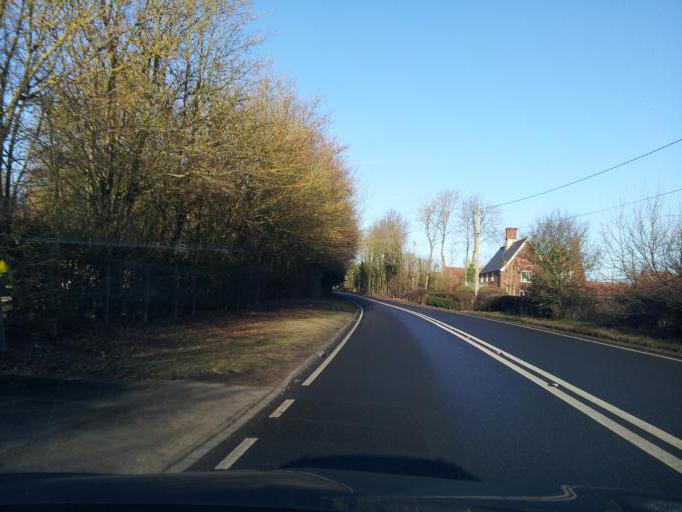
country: GB
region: England
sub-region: Suffolk
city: Lavenham
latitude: 52.1392
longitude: 0.7589
